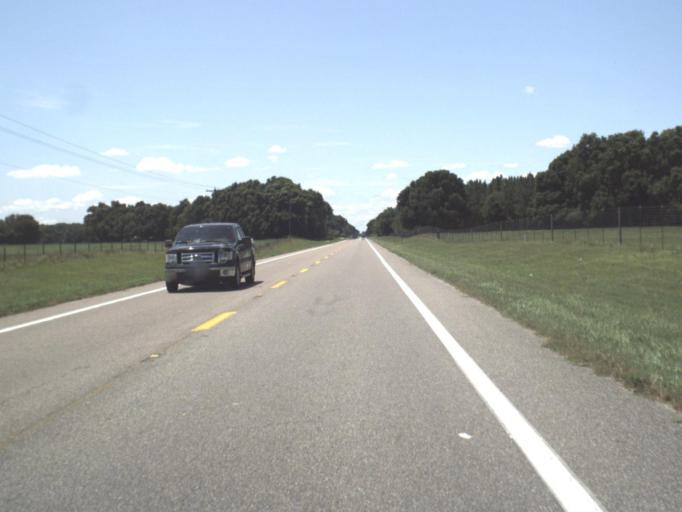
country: US
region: Florida
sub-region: Lafayette County
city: Mayo
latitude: 30.0223
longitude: -83.0489
